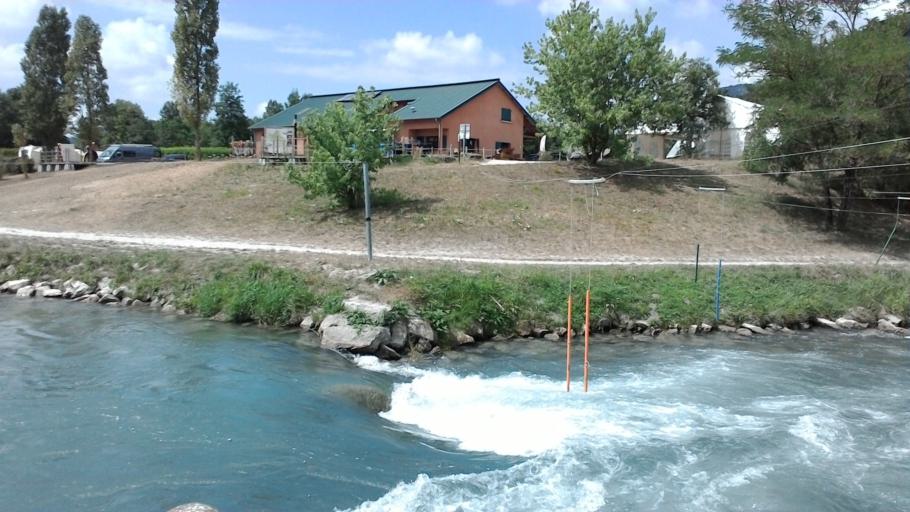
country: FR
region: Rhone-Alpes
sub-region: Departement de l'Ain
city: Sault-Brenaz
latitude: 45.8500
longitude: 5.4139
